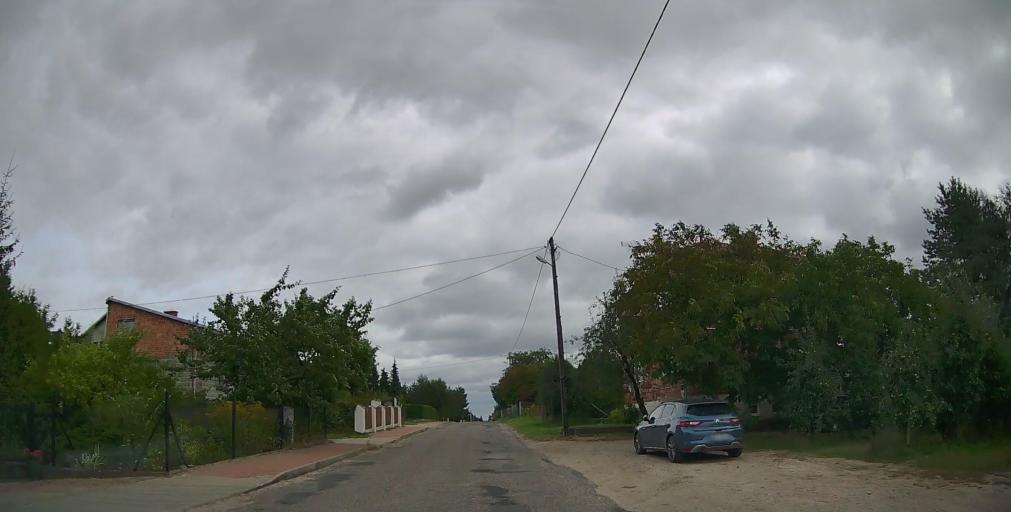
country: PL
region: Masovian Voivodeship
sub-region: Powiat grojecki
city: Belsk Duzy
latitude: 51.8183
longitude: 20.8237
